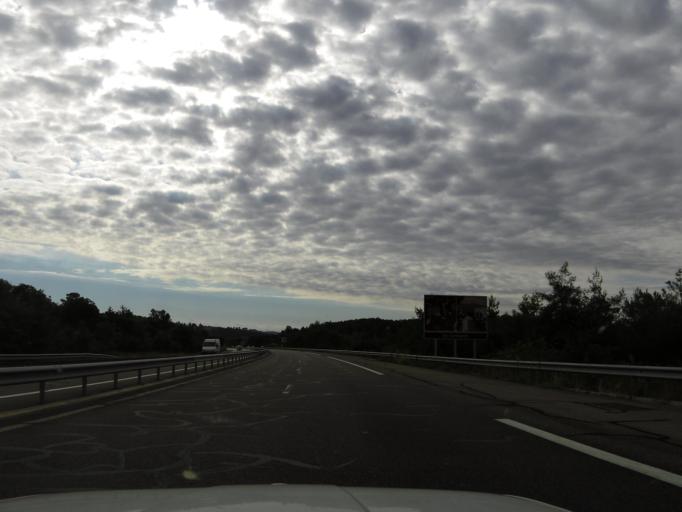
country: FR
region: Languedoc-Roussillon
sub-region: Departement du Gard
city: Vezenobres
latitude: 44.0464
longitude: 4.1271
